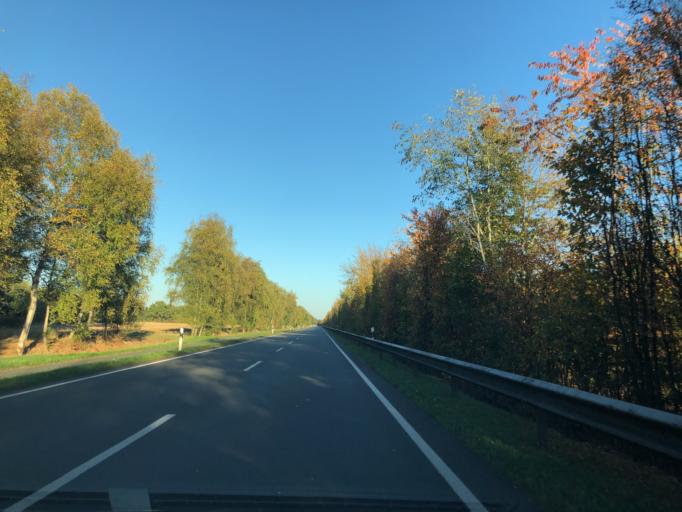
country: DE
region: Lower Saxony
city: Hilkenbrook
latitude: 53.0213
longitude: 7.7106
